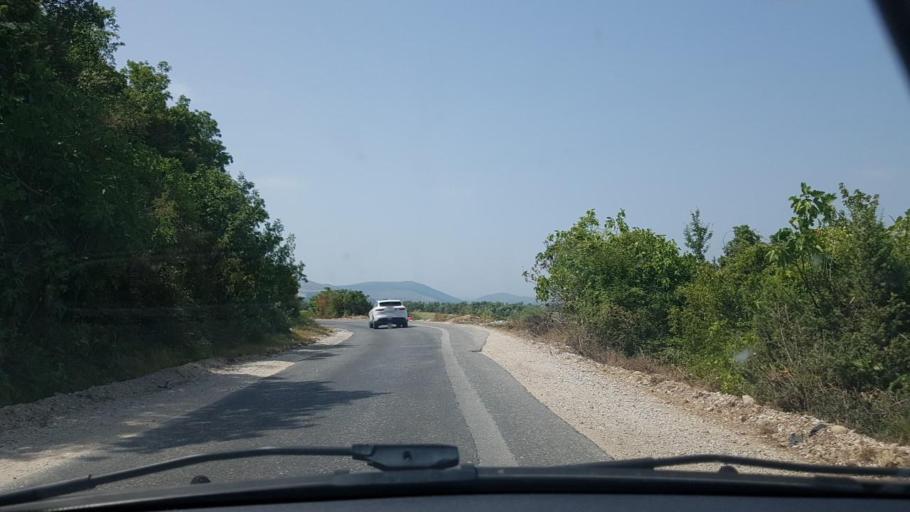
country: BA
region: Federation of Bosnia and Herzegovina
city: Tasovcici
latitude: 43.0317
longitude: 17.7392
